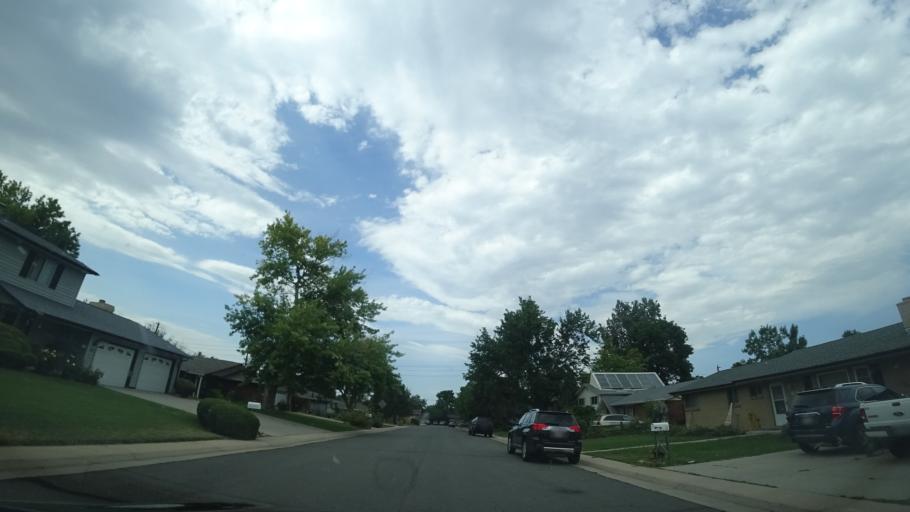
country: US
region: Colorado
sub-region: Jefferson County
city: Lakewood
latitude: 39.7086
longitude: -105.1029
